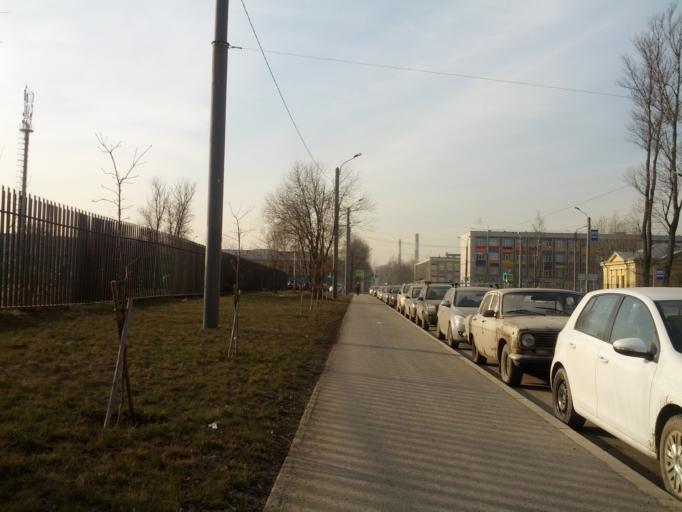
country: RU
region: Leningrad
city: Kalininskiy
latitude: 59.9630
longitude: 30.4004
